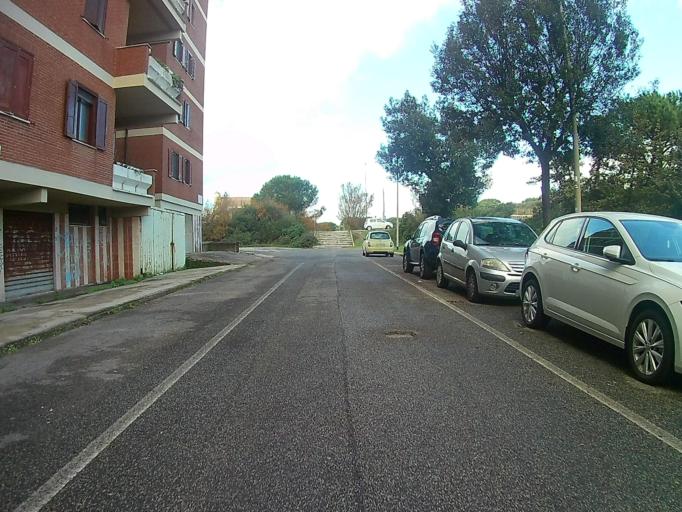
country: IT
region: Latium
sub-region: Citta metropolitana di Roma Capitale
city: Lido di Ostia
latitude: 41.7209
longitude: 12.3074
